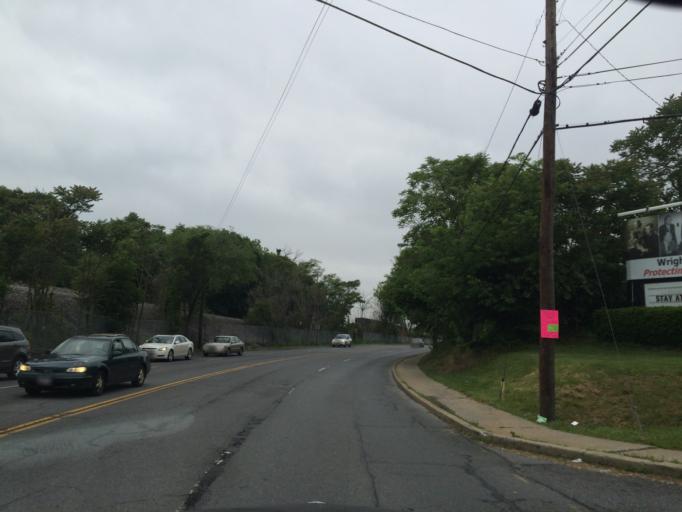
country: US
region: Maryland
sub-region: Washington County
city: Hagerstown
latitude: 39.6446
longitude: -77.7277
